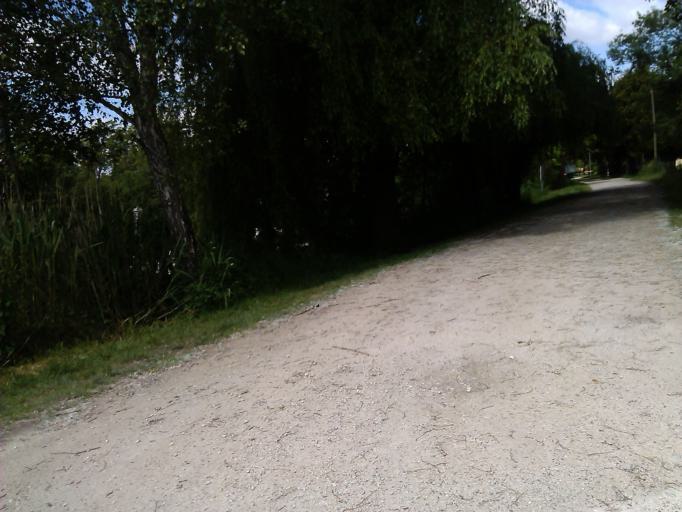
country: FR
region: Poitou-Charentes
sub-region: Departement de la Charente
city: Fleac
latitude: 45.6680
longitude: 0.1143
